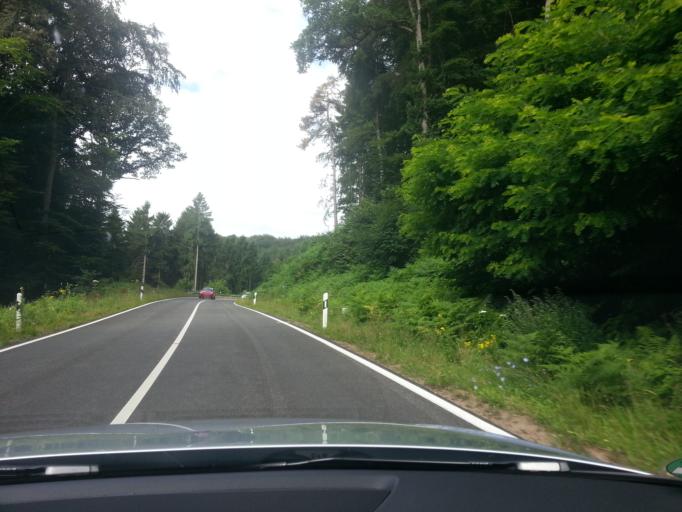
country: DE
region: Saarland
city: Losheim
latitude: 49.4721
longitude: 6.7968
